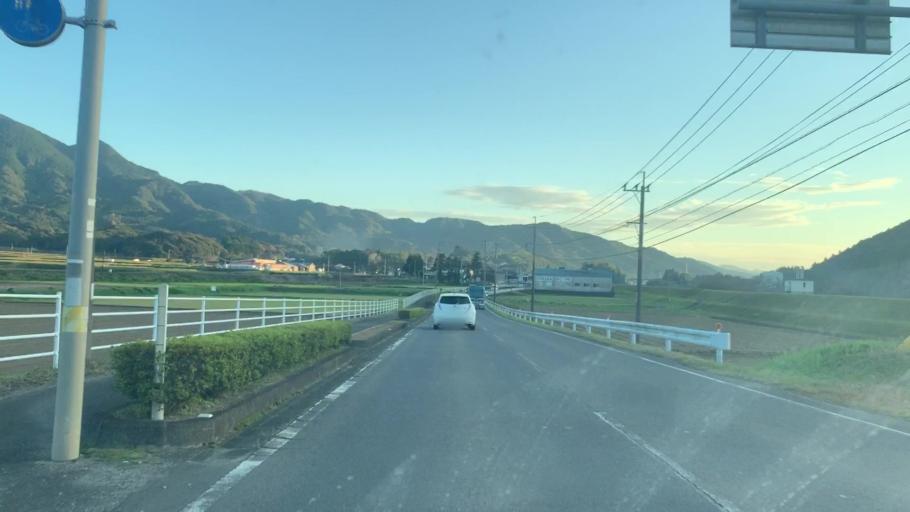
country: JP
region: Saga Prefecture
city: Imaricho-ko
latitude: 33.2992
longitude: 129.9699
